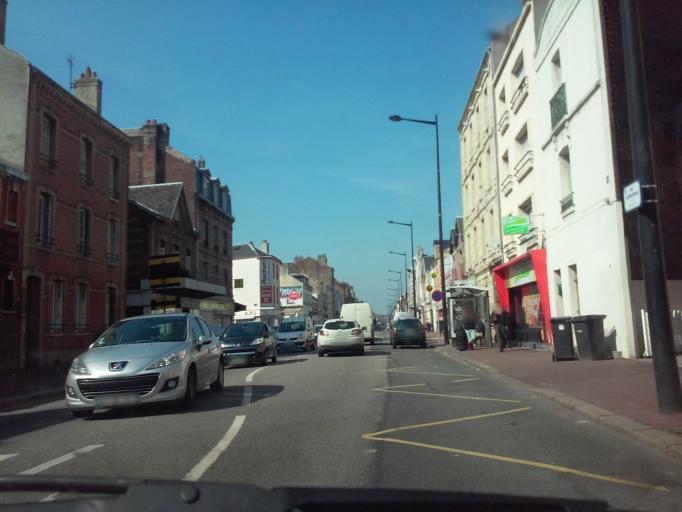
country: FR
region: Haute-Normandie
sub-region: Departement de la Seine-Maritime
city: Fontaine-la-Mallet
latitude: 49.5011
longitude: 0.1452
